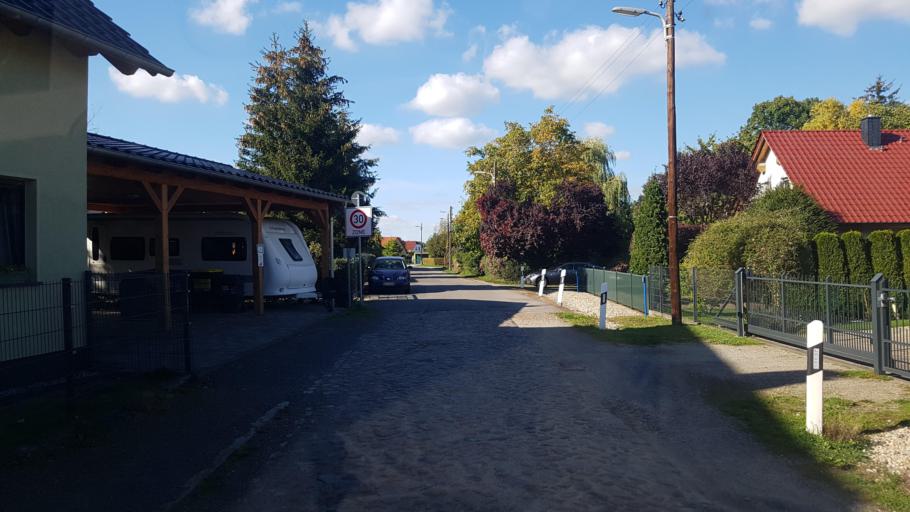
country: DE
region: Brandenburg
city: Cottbus
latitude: 51.7567
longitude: 14.2984
